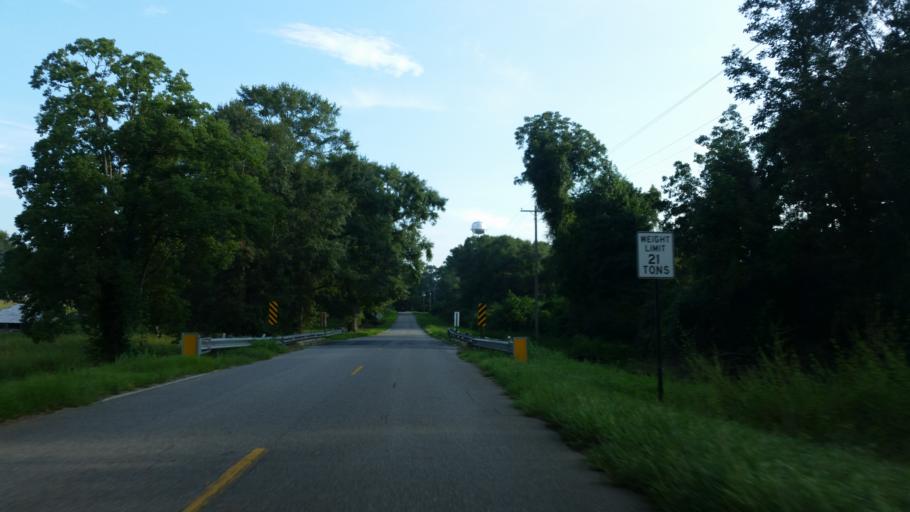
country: US
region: Alabama
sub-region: Escambia County
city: Atmore
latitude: 30.9874
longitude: -87.5713
